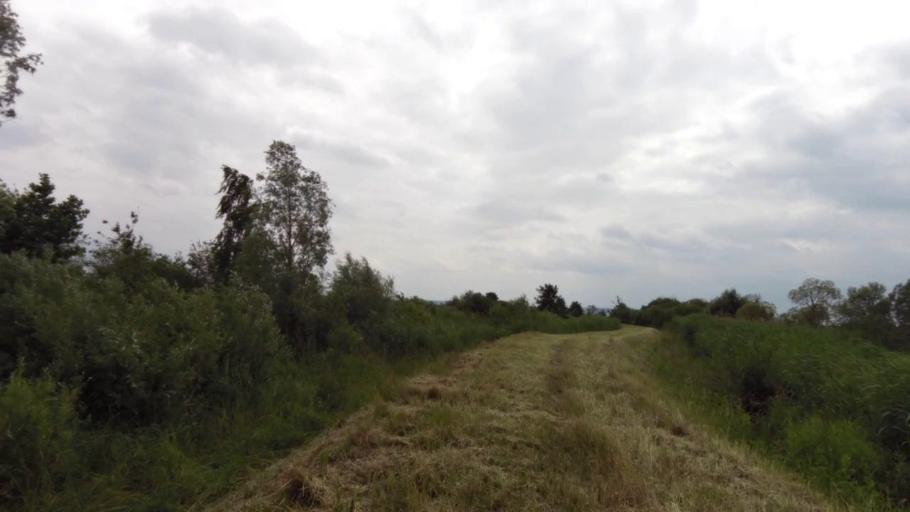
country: PL
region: West Pomeranian Voivodeship
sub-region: Szczecin
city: Szczecin
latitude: 53.4270
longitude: 14.6550
